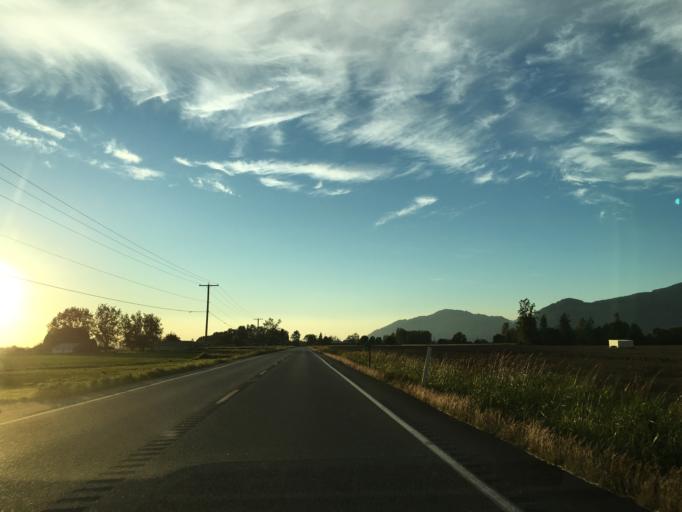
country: US
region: Washington
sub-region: Skagit County
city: Burlington
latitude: 48.5542
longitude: -122.4139
